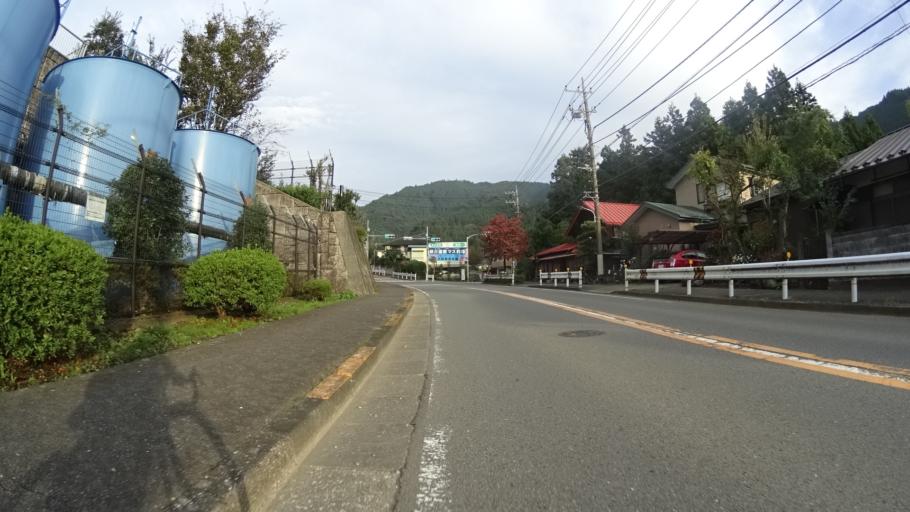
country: JP
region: Tokyo
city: Itsukaichi
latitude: 35.7290
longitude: 139.2035
